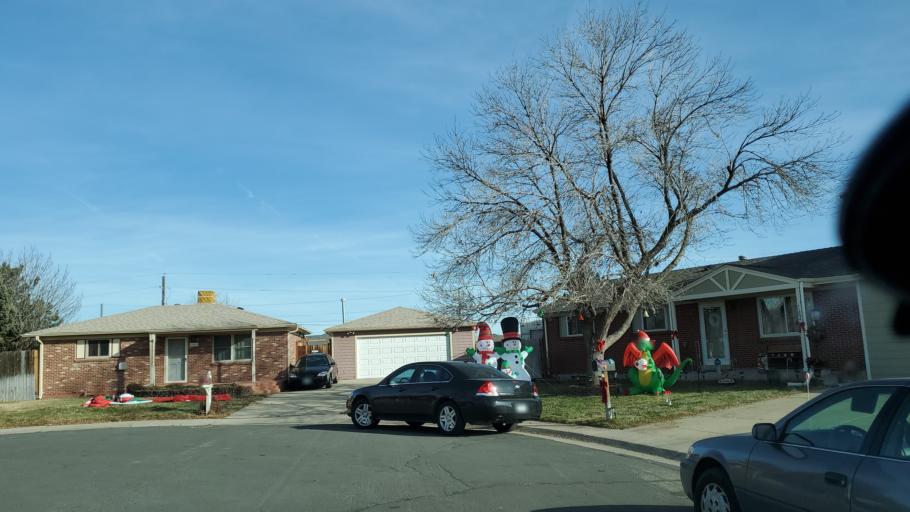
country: US
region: Colorado
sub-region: Adams County
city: Northglenn
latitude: 39.9121
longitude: -104.9597
